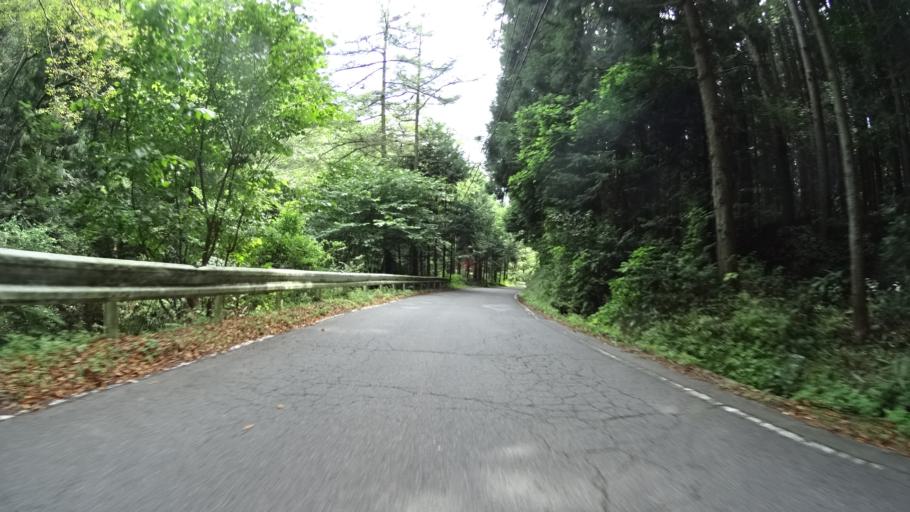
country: JP
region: Yamanashi
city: Nirasaki
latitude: 35.7763
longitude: 138.5347
